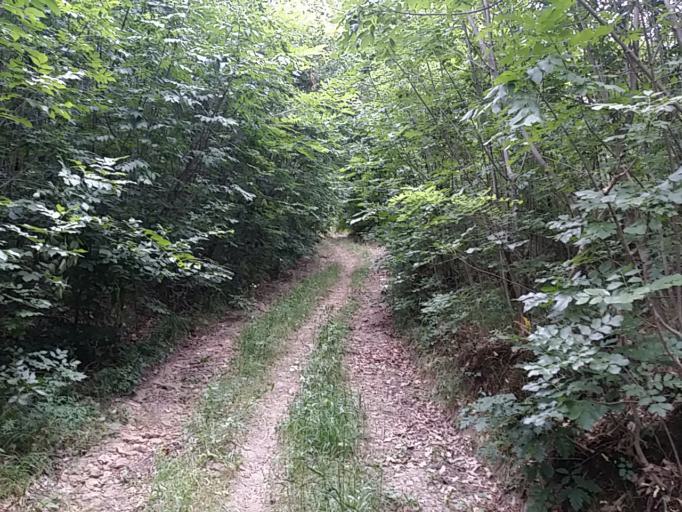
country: HU
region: Pest
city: Csobanka
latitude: 47.6536
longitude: 18.9463
